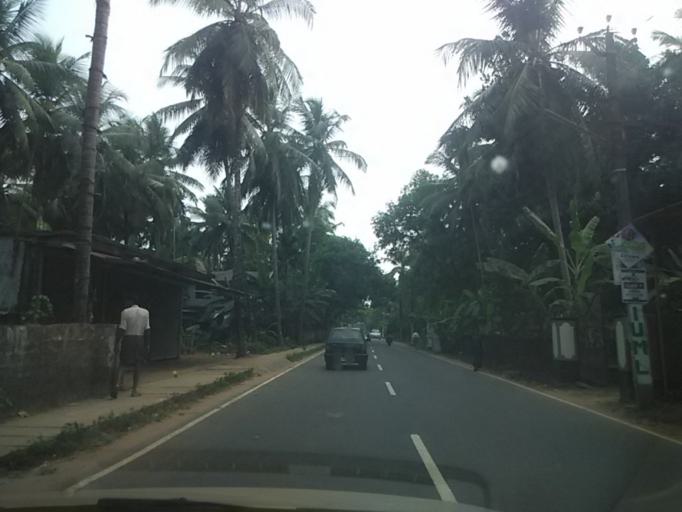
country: IN
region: Kerala
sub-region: Kozhikode
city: Naduvannur
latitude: 11.5031
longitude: 75.7732
